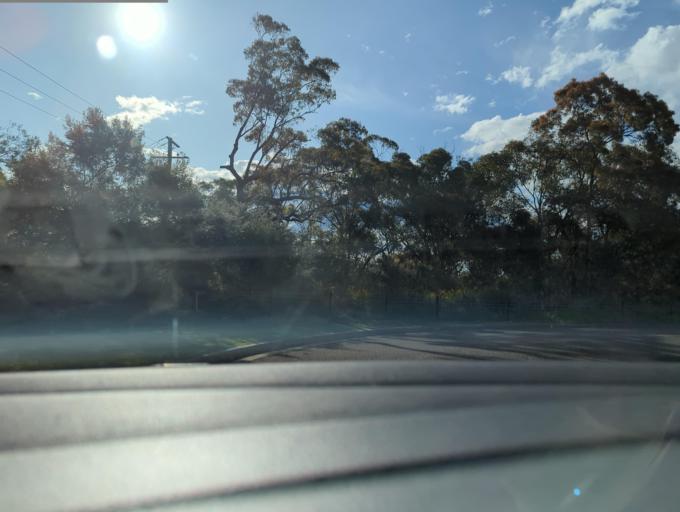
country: AU
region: New South Wales
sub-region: Sutherland Shire
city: Menai
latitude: -34.0285
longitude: 151.0031
